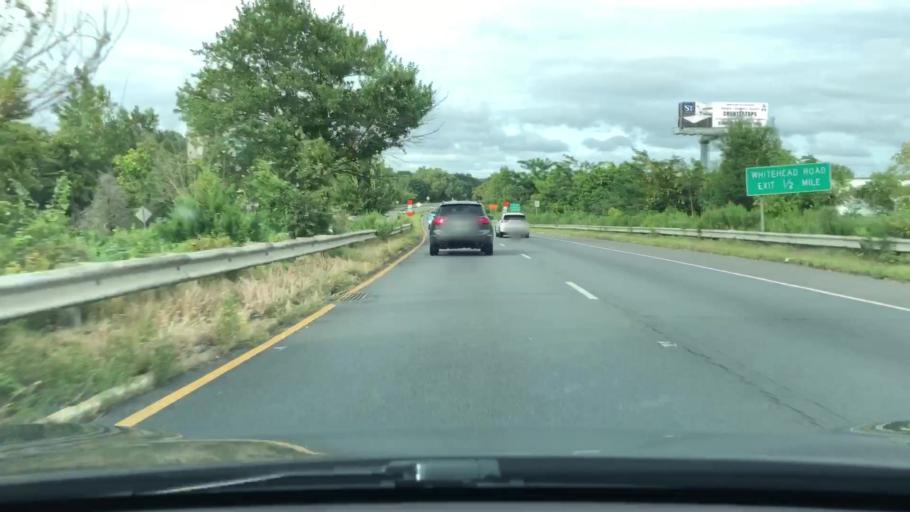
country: US
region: New Jersey
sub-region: Mercer County
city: Trenton
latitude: 40.2422
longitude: -74.7365
